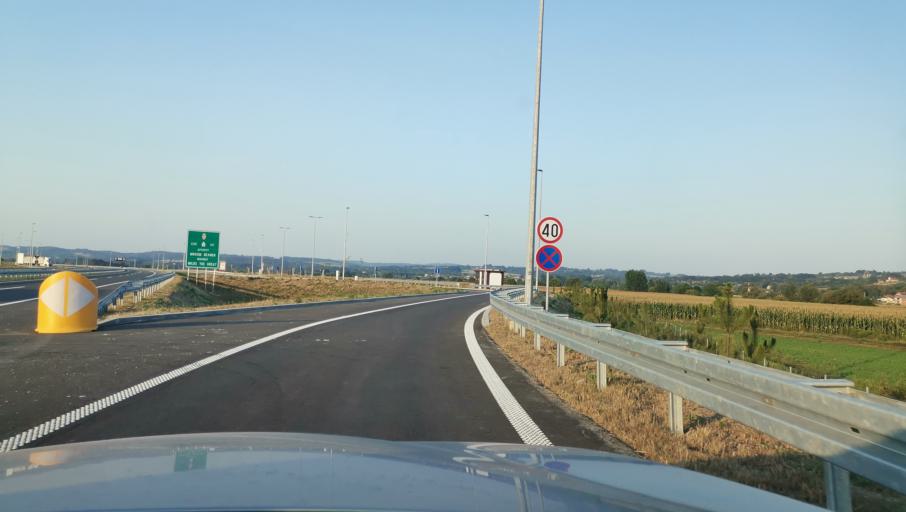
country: RS
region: Central Serbia
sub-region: Kolubarski Okrug
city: Ljig
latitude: 44.2405
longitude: 20.2615
